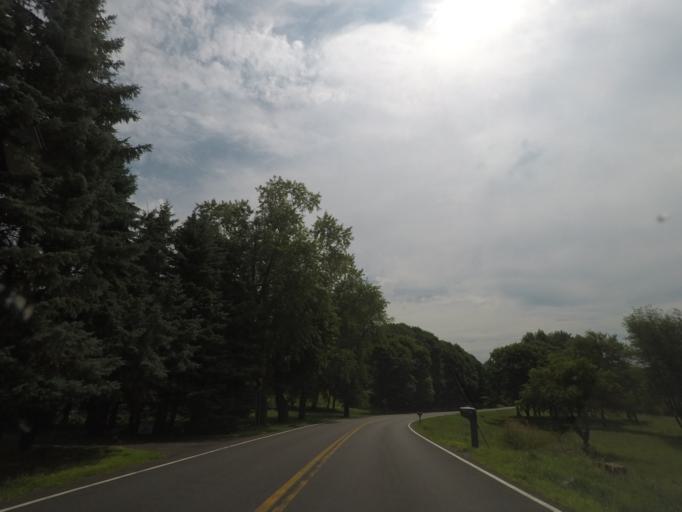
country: US
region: New York
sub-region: Saratoga County
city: Waterford
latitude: 42.7670
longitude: -73.6291
